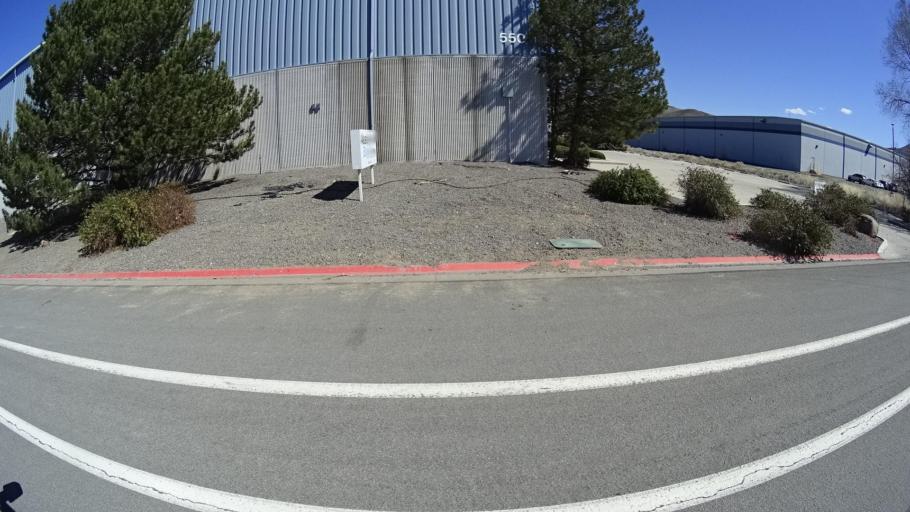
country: US
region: Nevada
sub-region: Washoe County
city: Sparks
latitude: 39.5376
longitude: -119.7111
